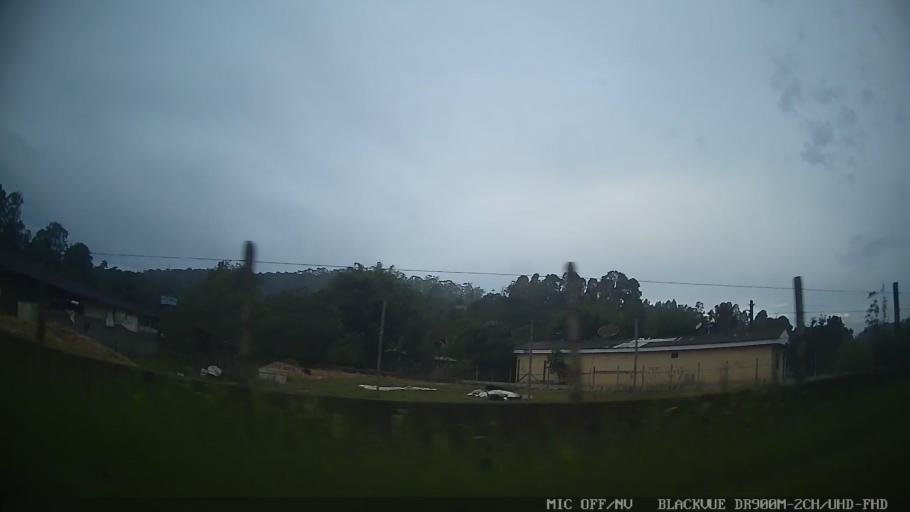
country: BR
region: Sao Paulo
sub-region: Rio Grande Da Serra
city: Rio Grande da Serra
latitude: -23.6866
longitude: -46.2991
